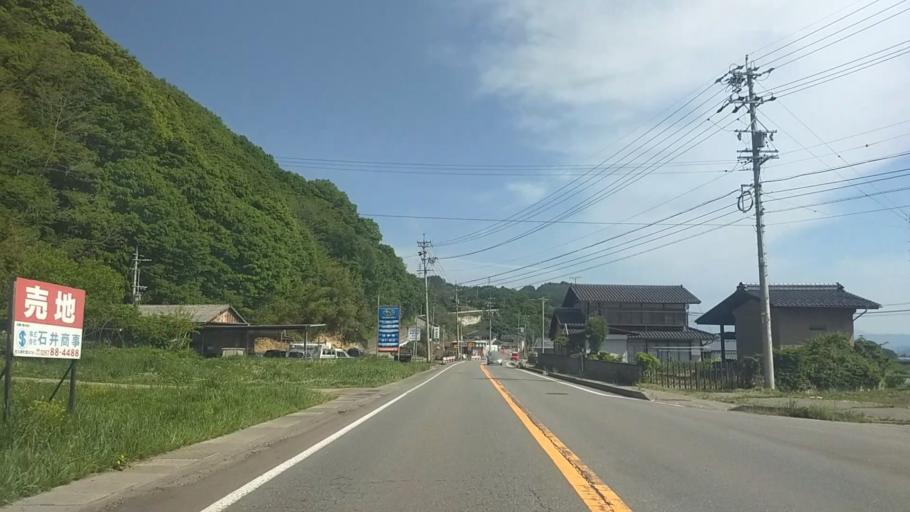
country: JP
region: Nagano
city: Saku
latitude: 36.1234
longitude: 138.4694
